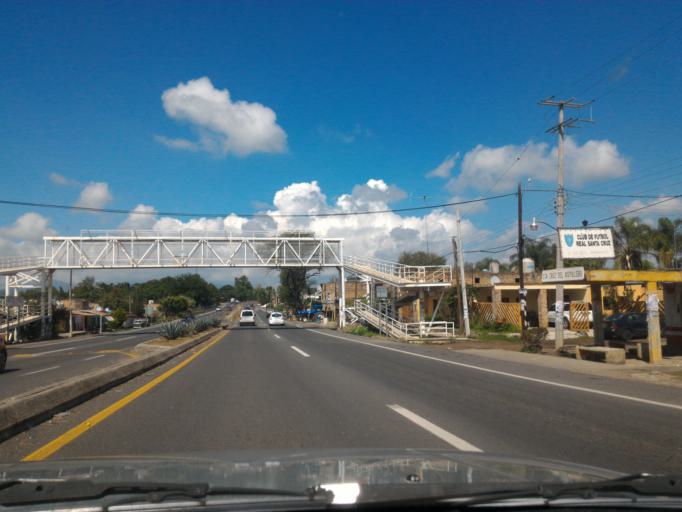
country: MX
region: Jalisco
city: Arenal
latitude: 20.7469
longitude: -103.6428
